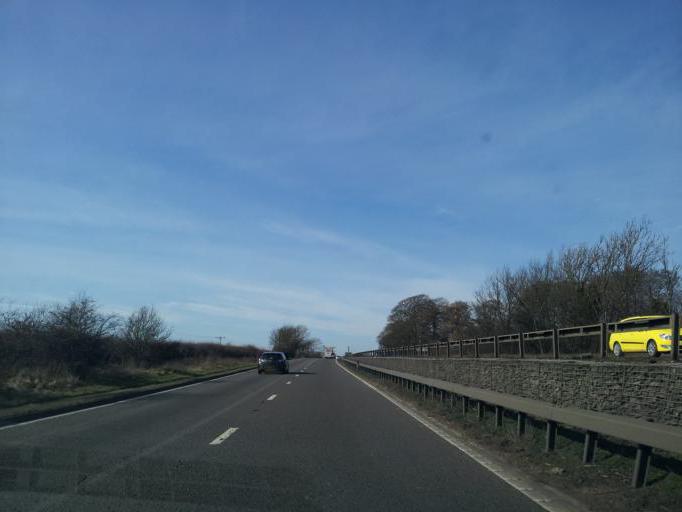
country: GB
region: England
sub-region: Peterborough
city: Wittering
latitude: 52.6220
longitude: -0.4570
